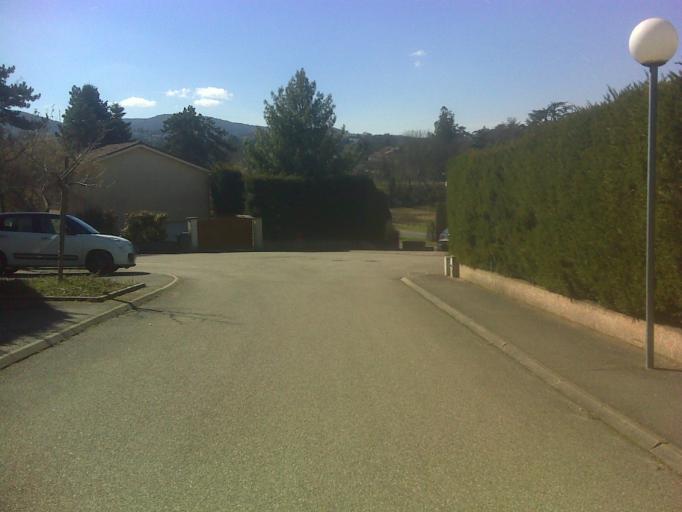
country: FR
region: Rhone-Alpes
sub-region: Departement du Rhone
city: Lentilly
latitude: 45.8224
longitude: 4.6696
